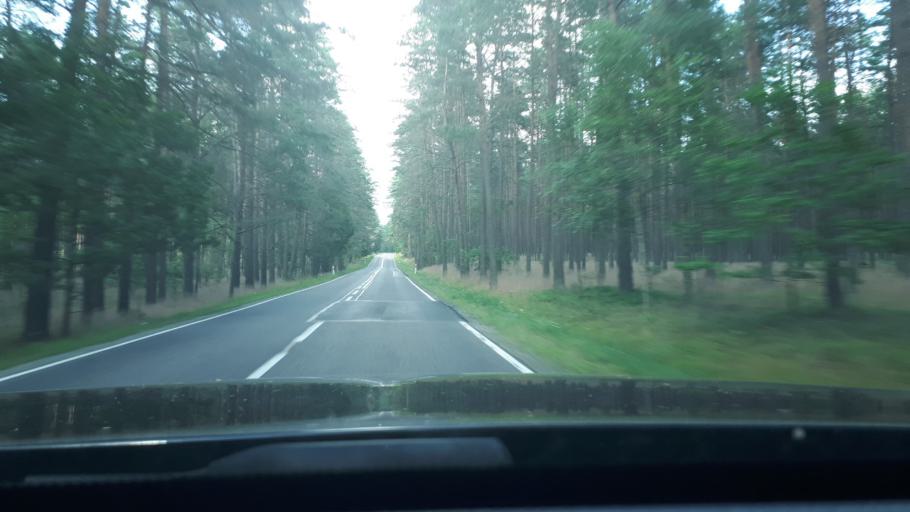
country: PL
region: Warmian-Masurian Voivodeship
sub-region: Powiat olsztynski
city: Stawiguda
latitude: 53.5380
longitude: 20.5279
